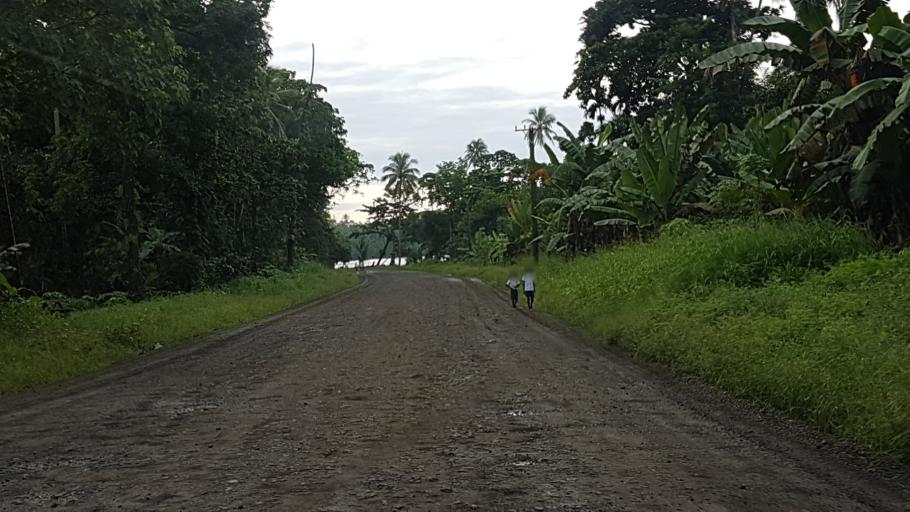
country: PG
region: Milne Bay
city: Alotau
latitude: -10.3256
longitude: 150.4986
